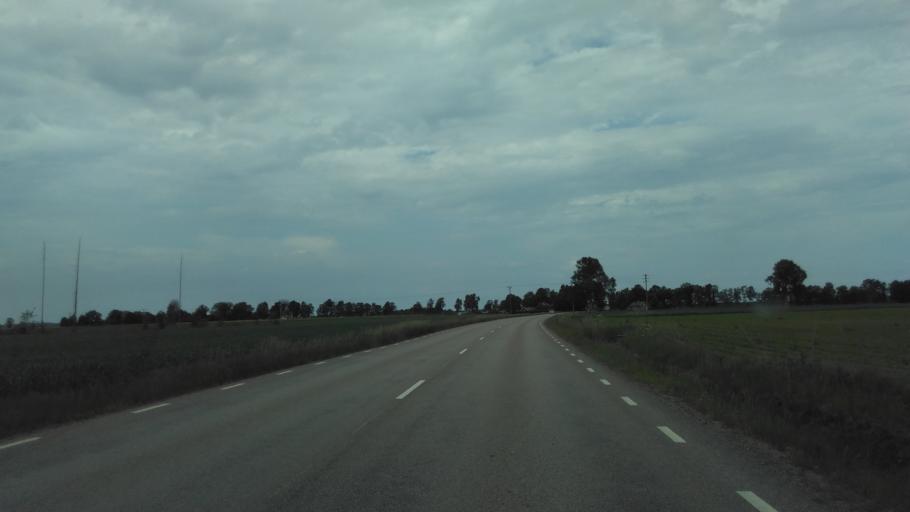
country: SE
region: Vaestra Goetaland
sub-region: Lidkopings Kommun
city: Lidkoping
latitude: 58.4426
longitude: 13.1616
